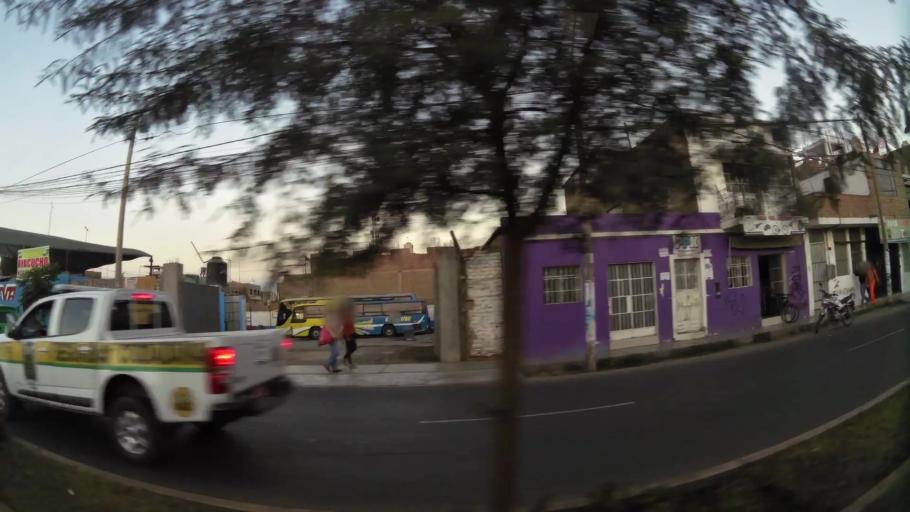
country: PE
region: Ica
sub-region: Provincia de Ica
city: Ica
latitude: -14.0664
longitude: -75.7324
